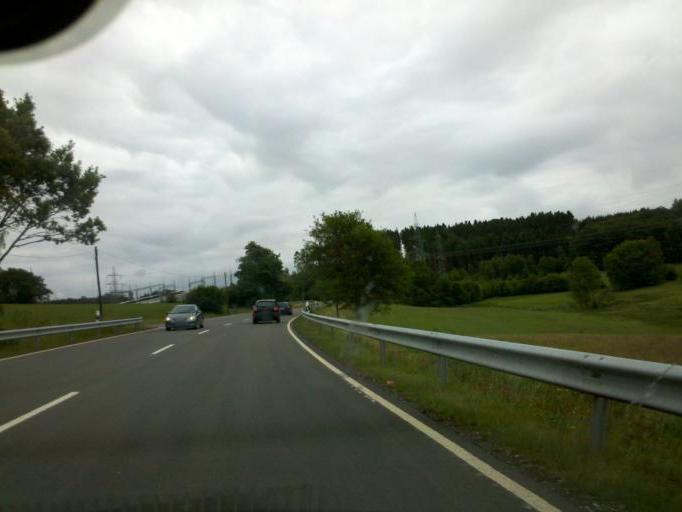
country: DE
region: North Rhine-Westphalia
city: Kreuztal
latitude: 51.0084
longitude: 7.9295
